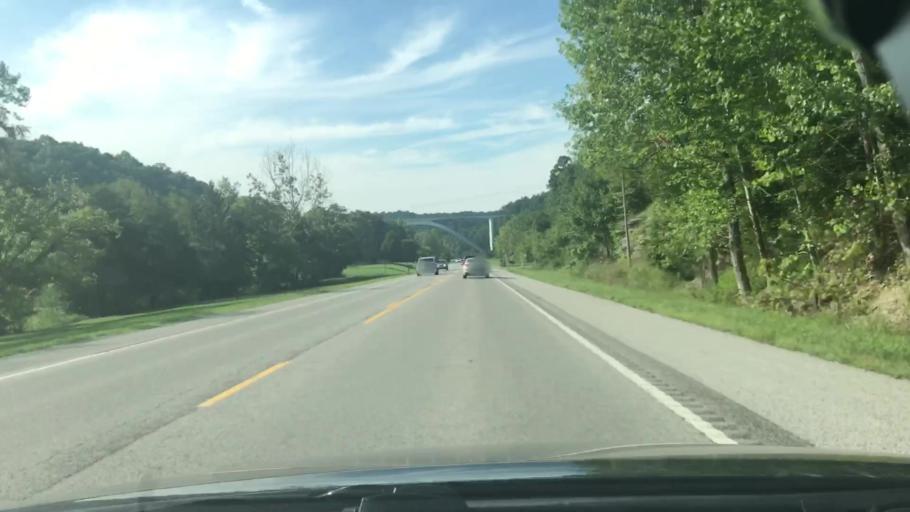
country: US
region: Tennessee
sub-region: Williamson County
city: Franklin
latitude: 35.9789
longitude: -86.9866
